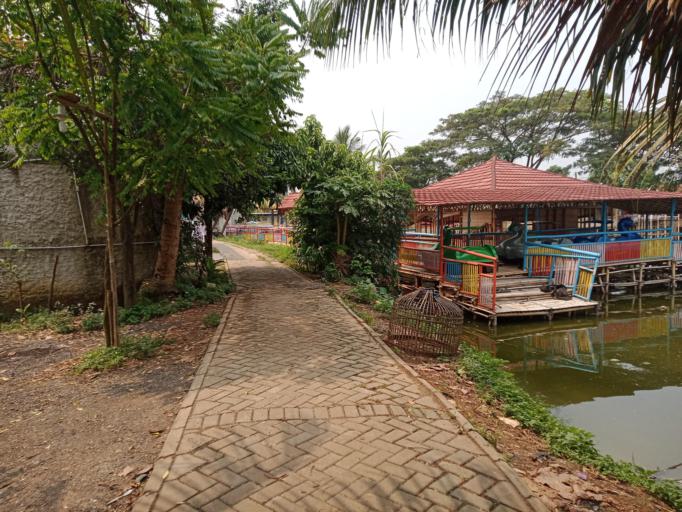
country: ID
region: West Java
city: Pasarkemis
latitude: -6.1981
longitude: 106.5254
